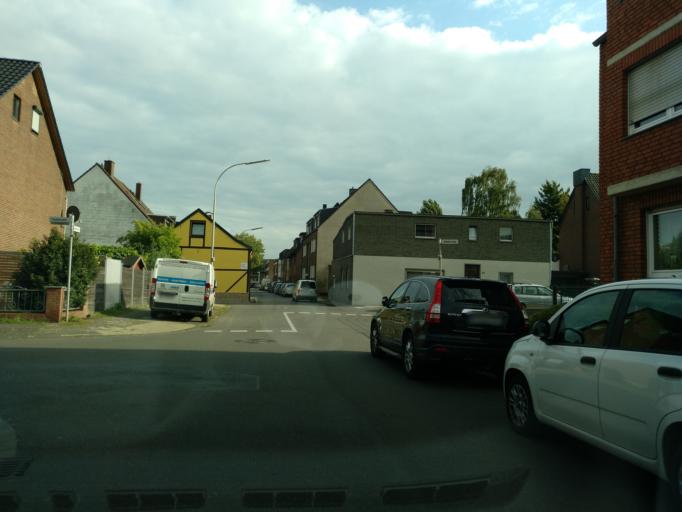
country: DE
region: North Rhine-Westphalia
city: Tonisvorst
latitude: 51.3694
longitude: 6.5158
